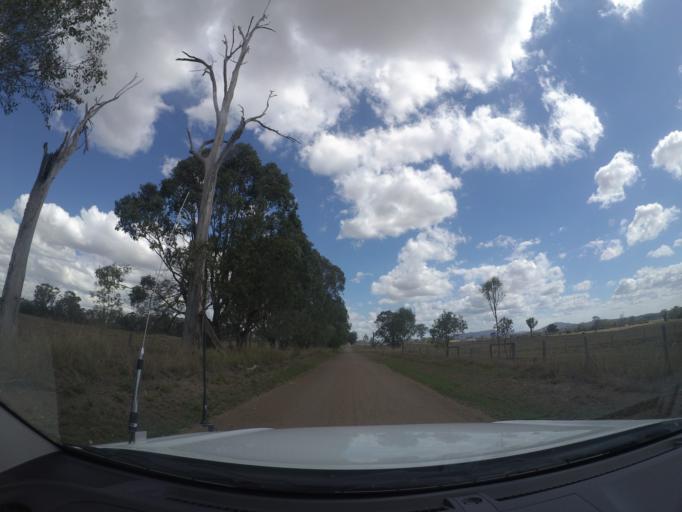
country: AU
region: Queensland
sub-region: Logan
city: Cedar Vale
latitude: -27.8893
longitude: 152.9598
